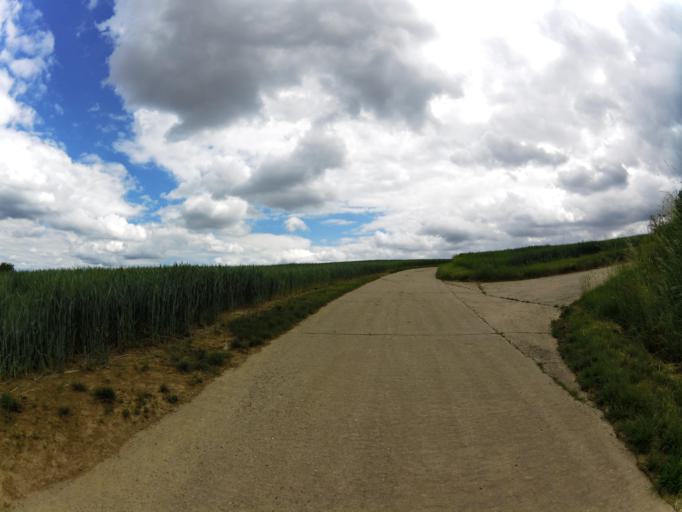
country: DE
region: Bavaria
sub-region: Regierungsbezirk Unterfranken
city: Winterhausen
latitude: 49.6727
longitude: 10.0063
